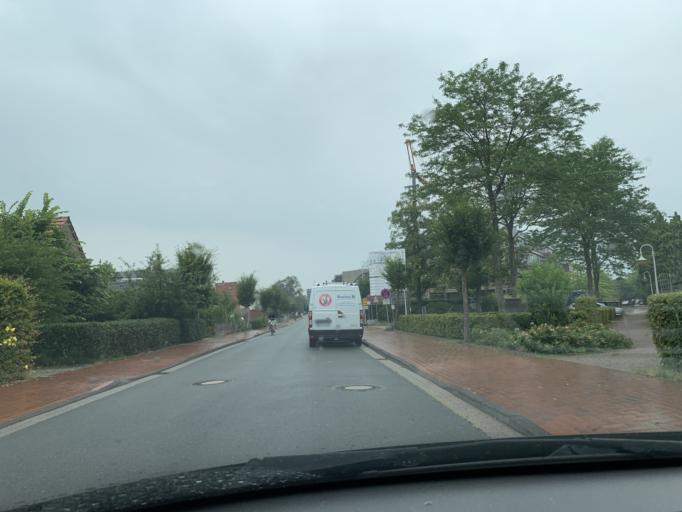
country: DE
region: Lower Saxony
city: Westerstede
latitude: 53.2519
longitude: 7.9262
